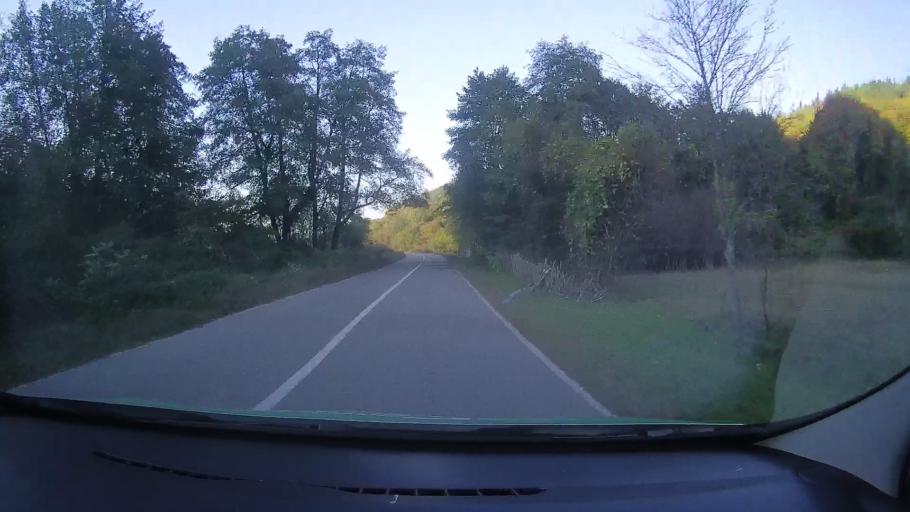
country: RO
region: Timis
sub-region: Comuna Fardea
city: Fardea
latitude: 45.7054
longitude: 22.1605
